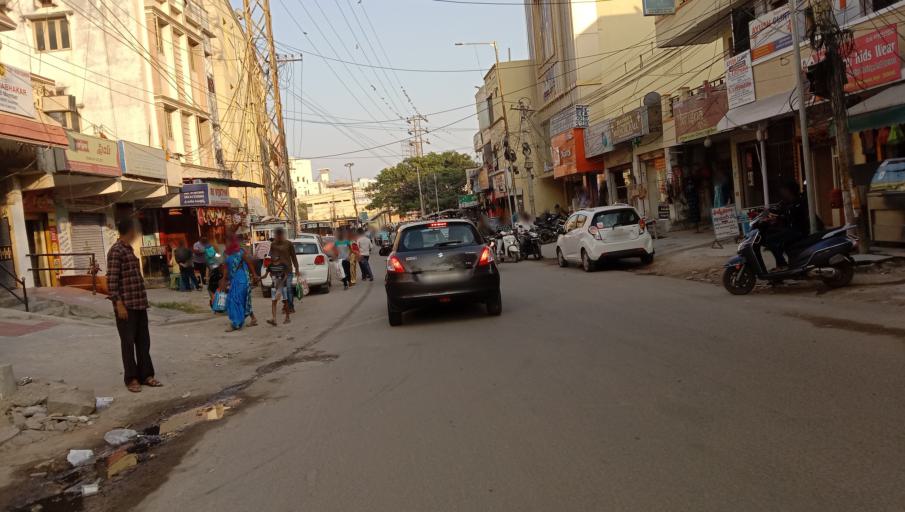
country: IN
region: Telangana
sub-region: Hyderabad
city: Hyderabad
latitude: 17.3641
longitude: 78.4257
